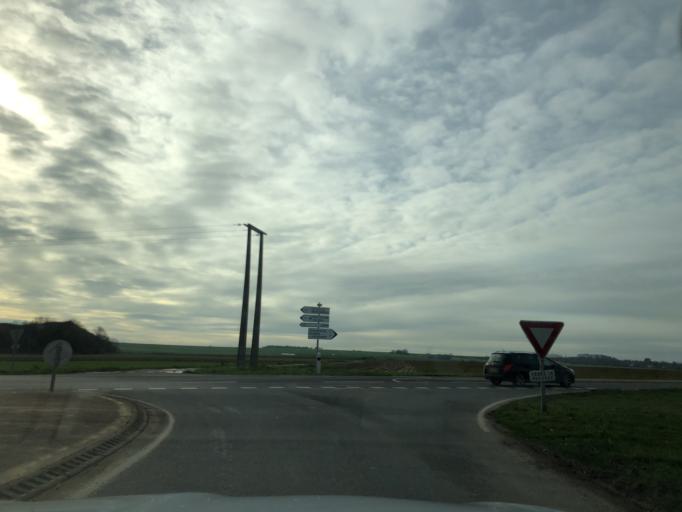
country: FR
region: Lower Normandy
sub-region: Departement du Calvados
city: Hermanville-sur-Mer
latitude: 49.2841
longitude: -0.3298
